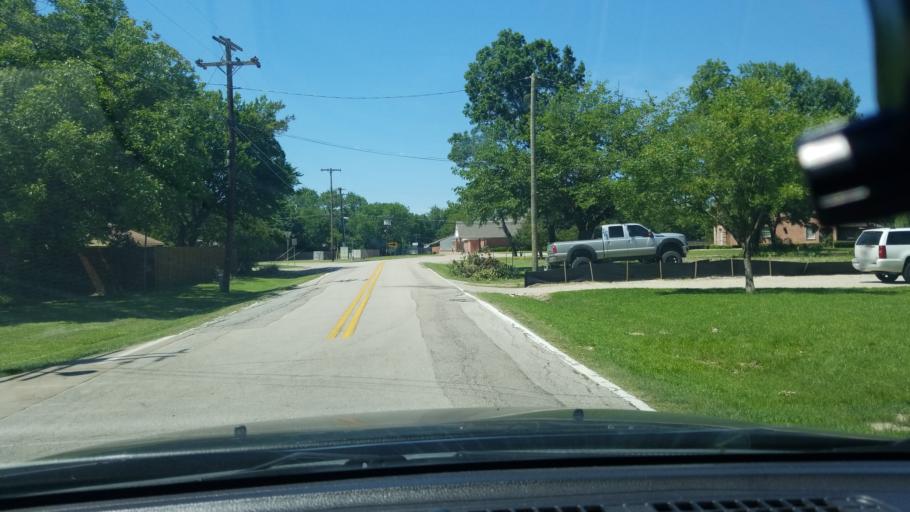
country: US
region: Texas
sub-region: Dallas County
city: Mesquite
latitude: 32.7606
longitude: -96.6052
